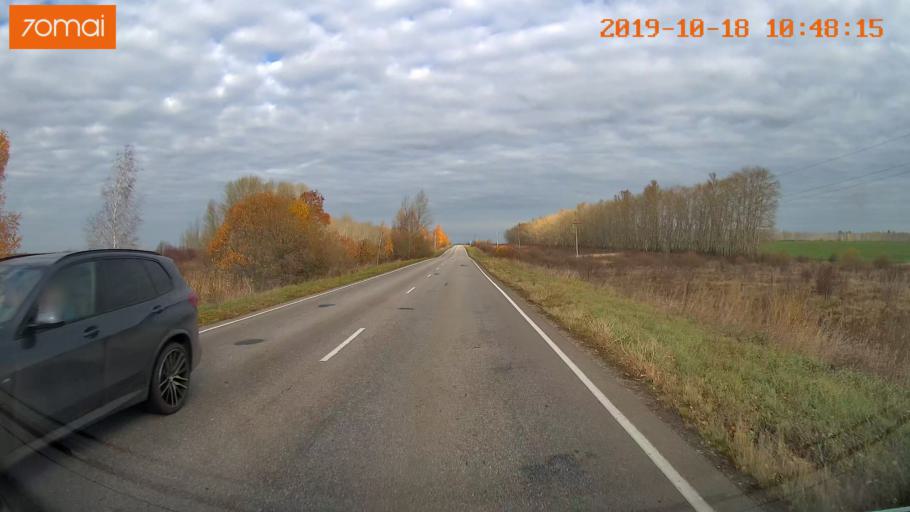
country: RU
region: Tula
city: Yepifan'
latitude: 53.7136
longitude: 38.6974
